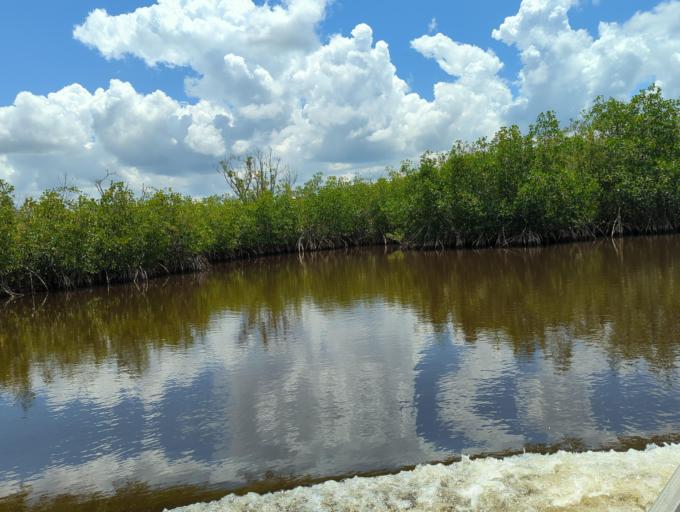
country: US
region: Florida
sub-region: Collier County
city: Marco
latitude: 25.9031
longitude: -81.3750
